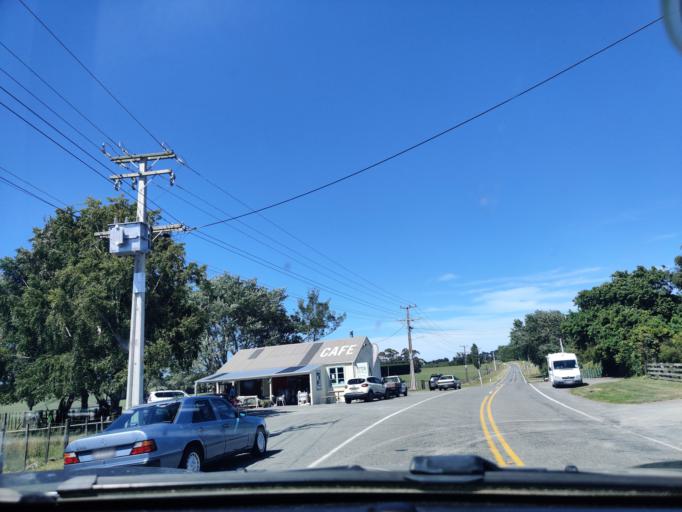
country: NZ
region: Wellington
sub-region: Upper Hutt City
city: Upper Hutt
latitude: -41.3525
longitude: 175.2056
